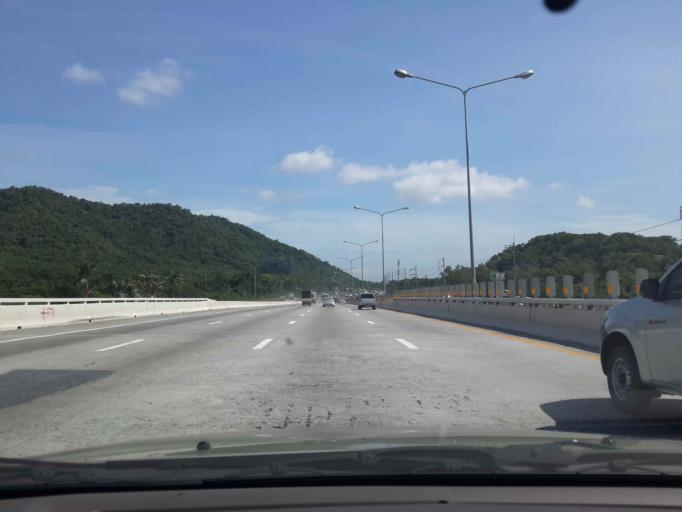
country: TH
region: Chon Buri
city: Si Racha
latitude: 13.2532
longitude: 100.9920
